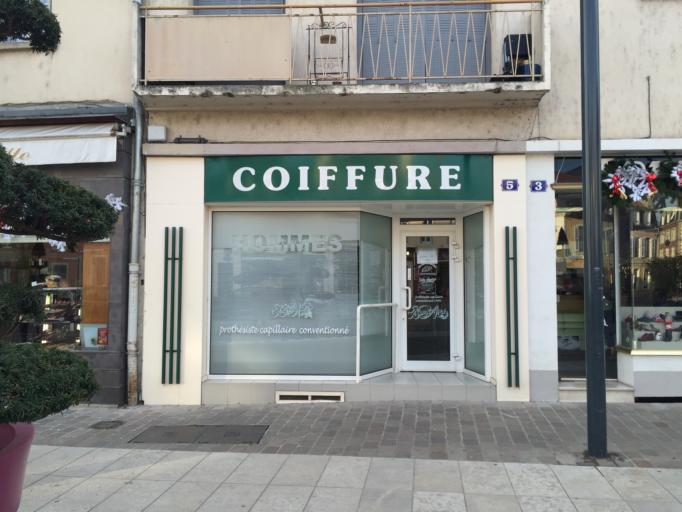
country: FR
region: Auvergne
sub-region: Departement de l'Allier
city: Moulins
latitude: 46.5633
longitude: 3.3305
